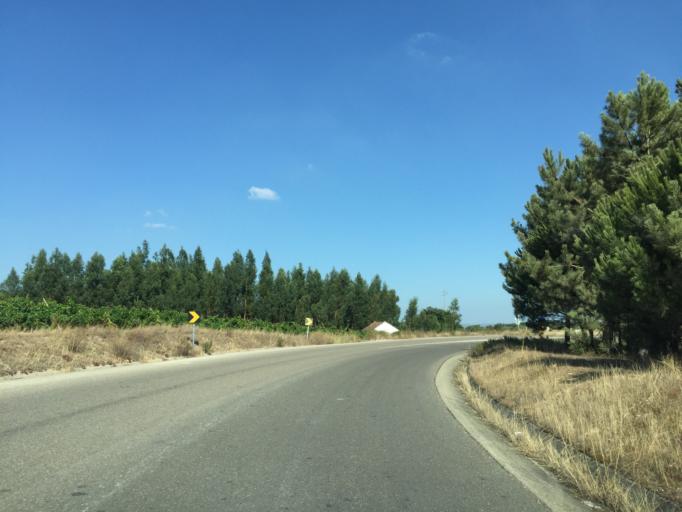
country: PT
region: Santarem
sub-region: Cartaxo
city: Pontevel
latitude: 39.1551
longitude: -8.8661
